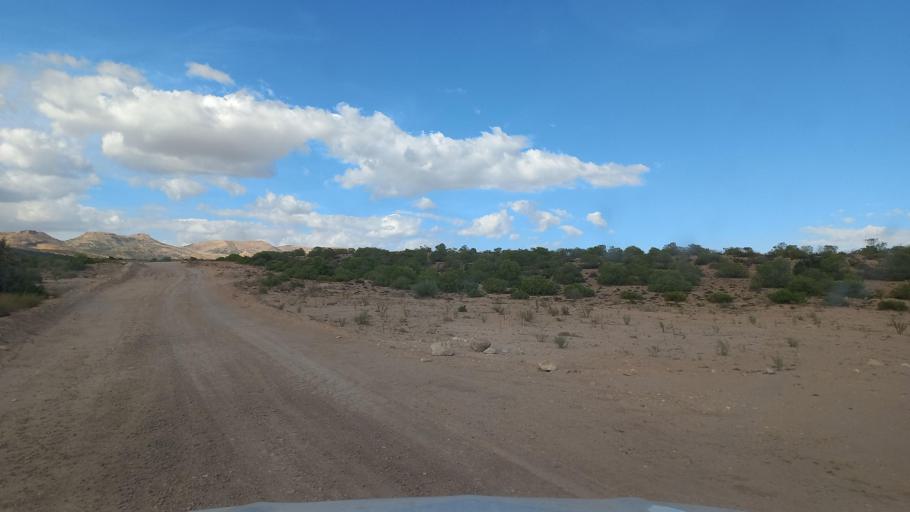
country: TN
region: Al Qasrayn
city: Sbiba
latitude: 35.3981
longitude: 9.0114
